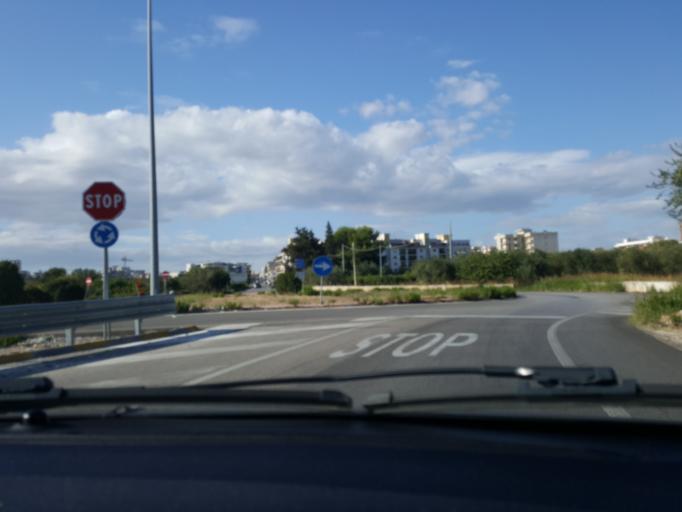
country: IT
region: Apulia
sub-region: Provincia di Bari
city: Triggiano
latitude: 41.0739
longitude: 16.9376
